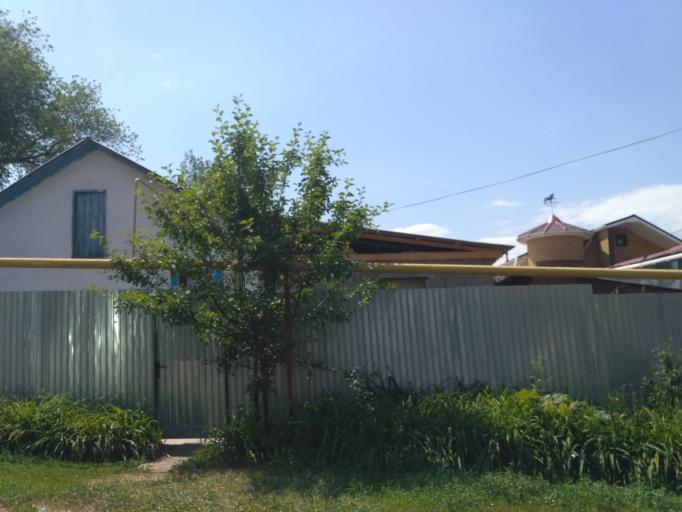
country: KZ
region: Almaty Oblysy
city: Burunday
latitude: 43.1908
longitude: 76.6192
